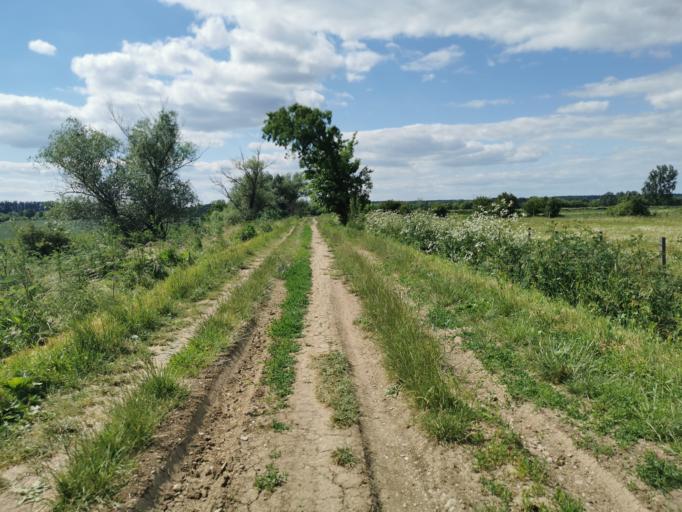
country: CZ
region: South Moravian
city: Rohatec
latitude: 48.8751
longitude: 17.2087
